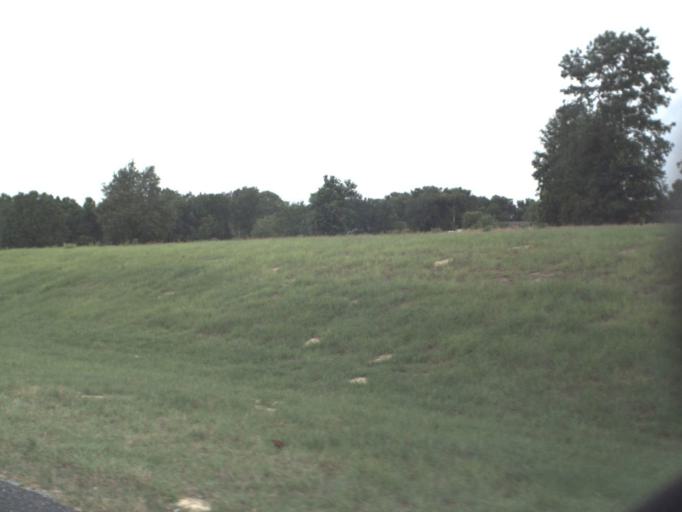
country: US
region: Florida
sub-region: Marion County
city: Belleview
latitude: 29.0284
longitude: -82.0215
